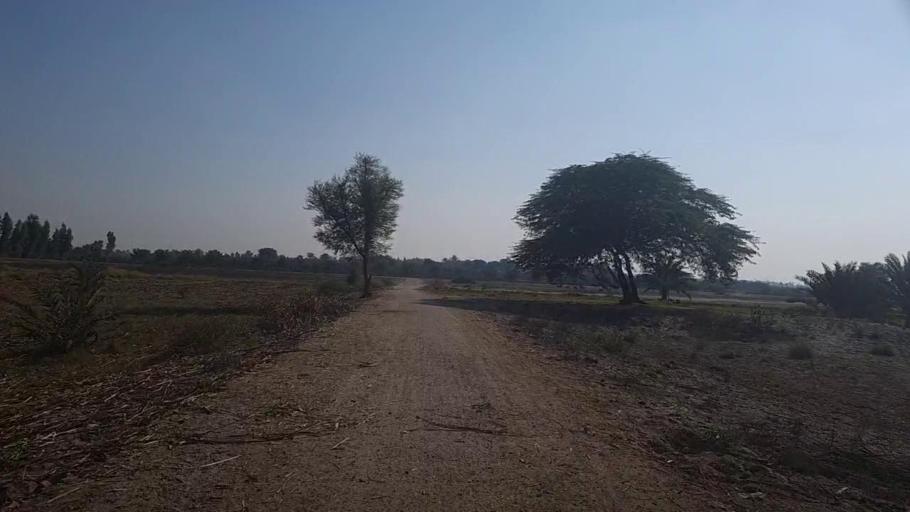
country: PK
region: Sindh
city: Kot Diji
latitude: 27.4310
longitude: 68.7339
